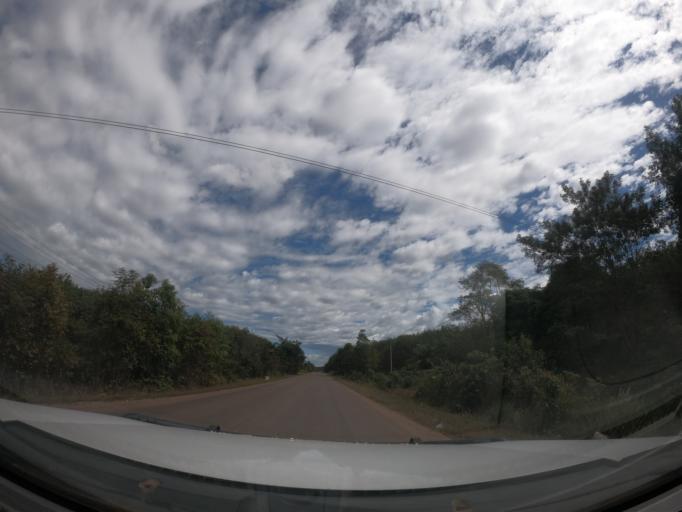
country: LA
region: Bolikhamxai
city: Muang Pakxan
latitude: 18.4437
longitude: 103.4996
